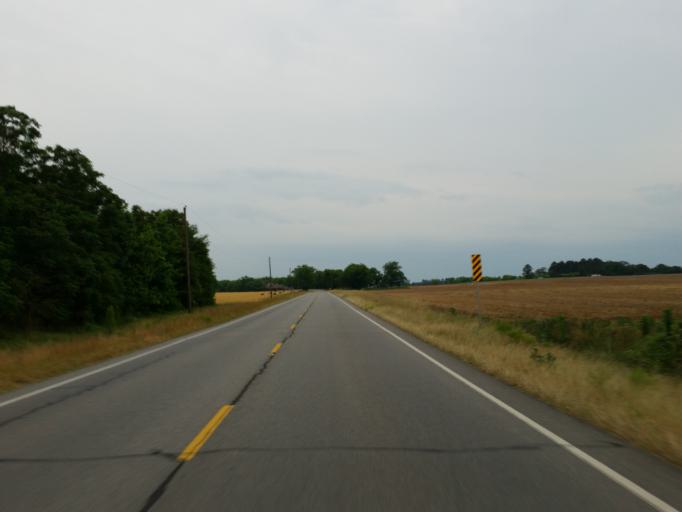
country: US
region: Georgia
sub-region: Dooly County
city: Unadilla
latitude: 32.2351
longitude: -83.7530
